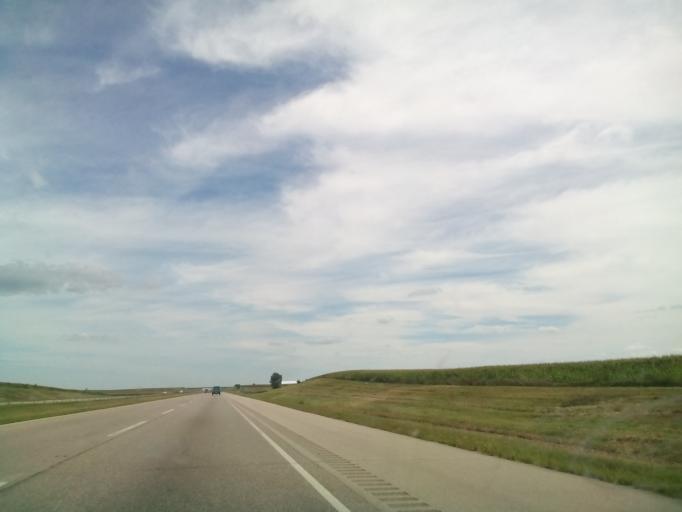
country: US
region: Illinois
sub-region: DeKalb County
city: Malta
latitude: 41.8994
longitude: -88.9251
